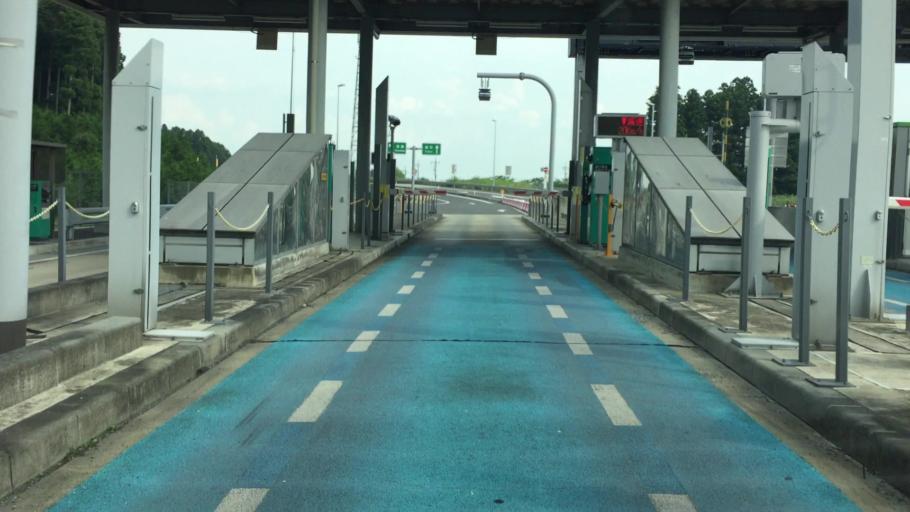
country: JP
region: Tochigi
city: Kuroiso
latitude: 36.9603
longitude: 139.9869
